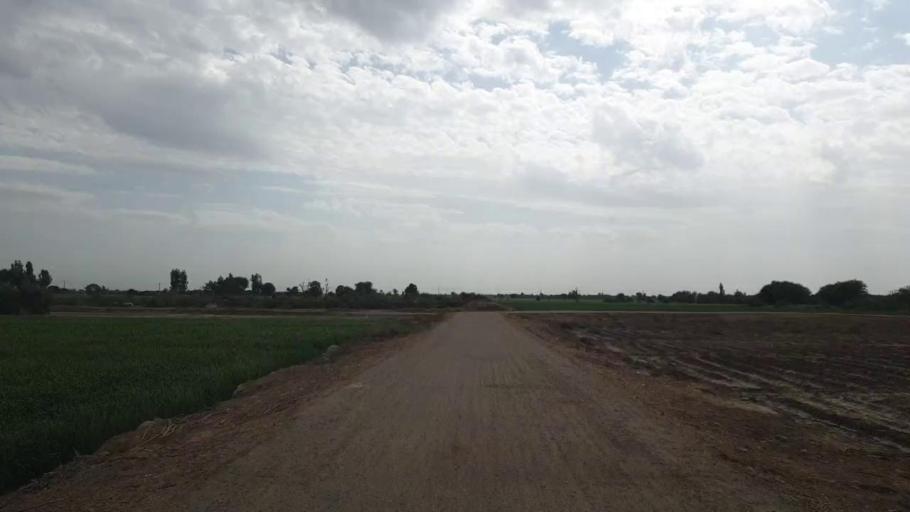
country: PK
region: Sindh
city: Hala
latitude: 25.9259
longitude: 68.4338
